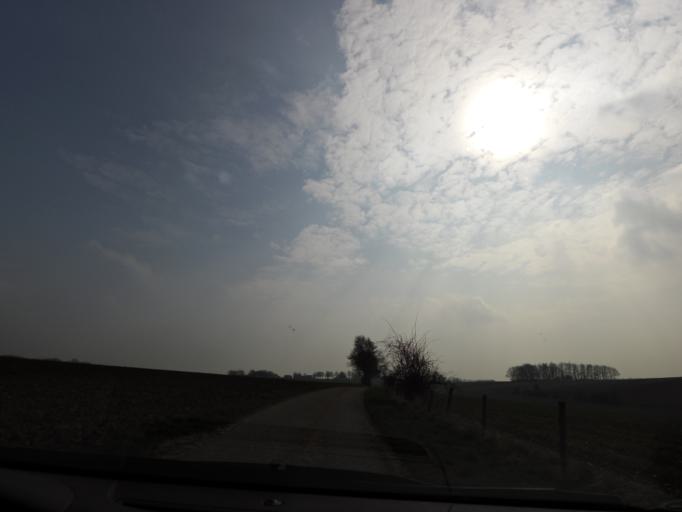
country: NL
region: Limburg
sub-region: Gemeente Voerendaal
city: Ubachsberg
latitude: 50.8446
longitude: 5.9282
